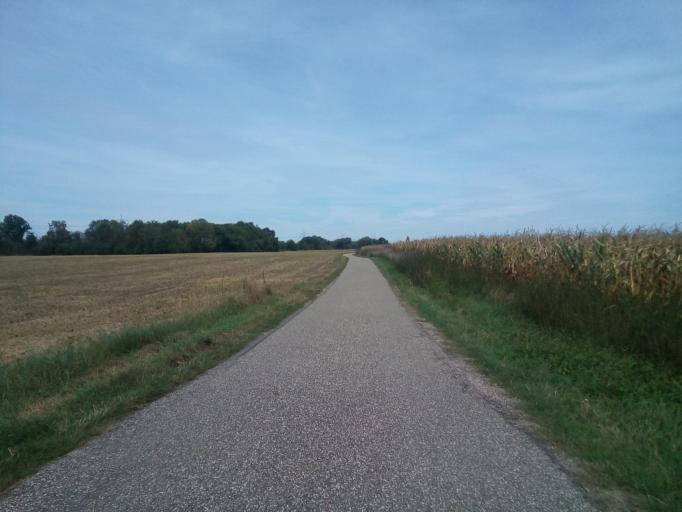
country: DE
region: Baden-Wuerttemberg
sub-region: Karlsruhe Region
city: Ottenhofen
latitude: 48.7289
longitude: 8.1190
